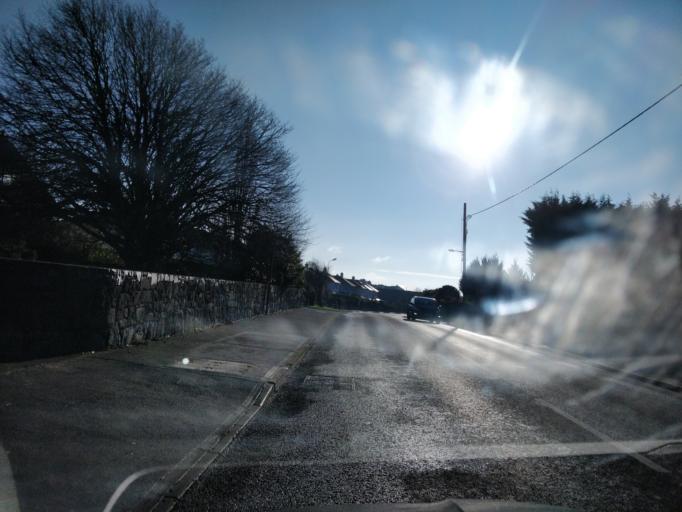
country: IE
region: Connaught
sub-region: County Galway
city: Bearna
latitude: 53.2650
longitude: -9.1059
